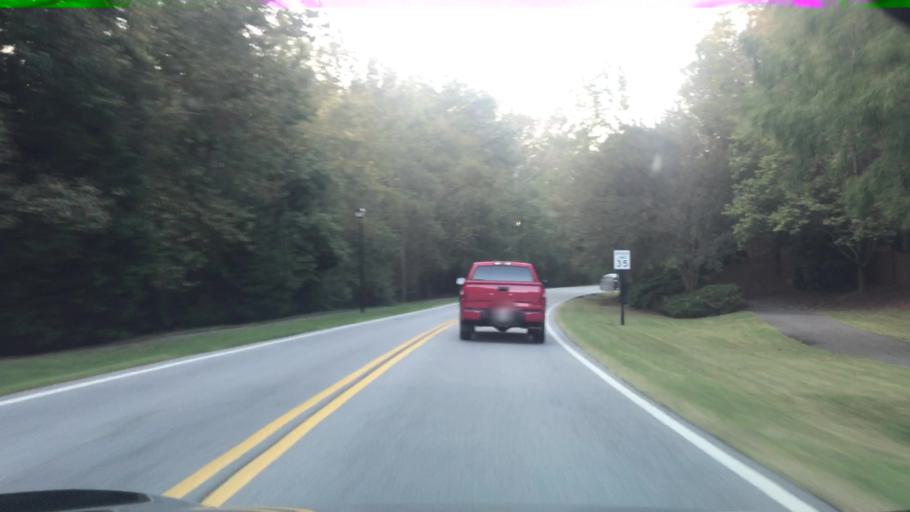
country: US
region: Georgia
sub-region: Gwinnett County
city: Suwanee
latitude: 34.0557
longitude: -84.0944
